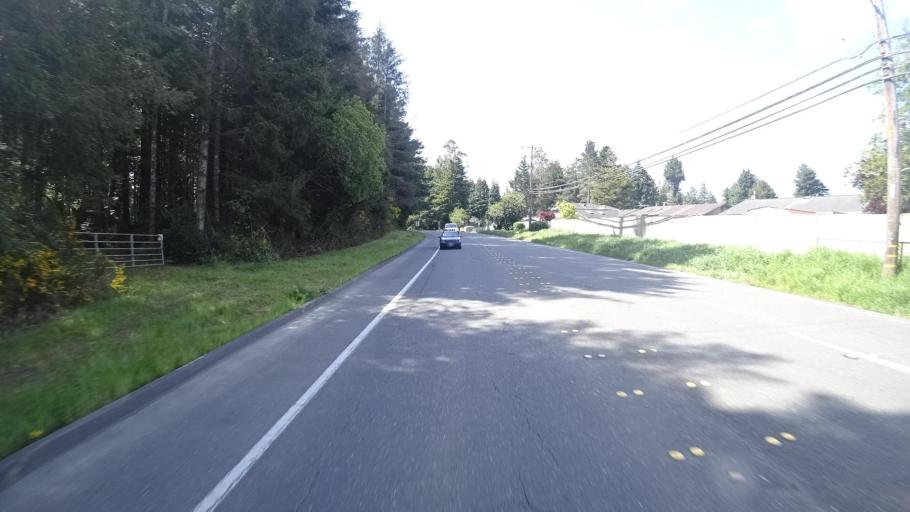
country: US
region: California
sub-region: Humboldt County
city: Cutten
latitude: 40.7575
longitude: -124.1467
